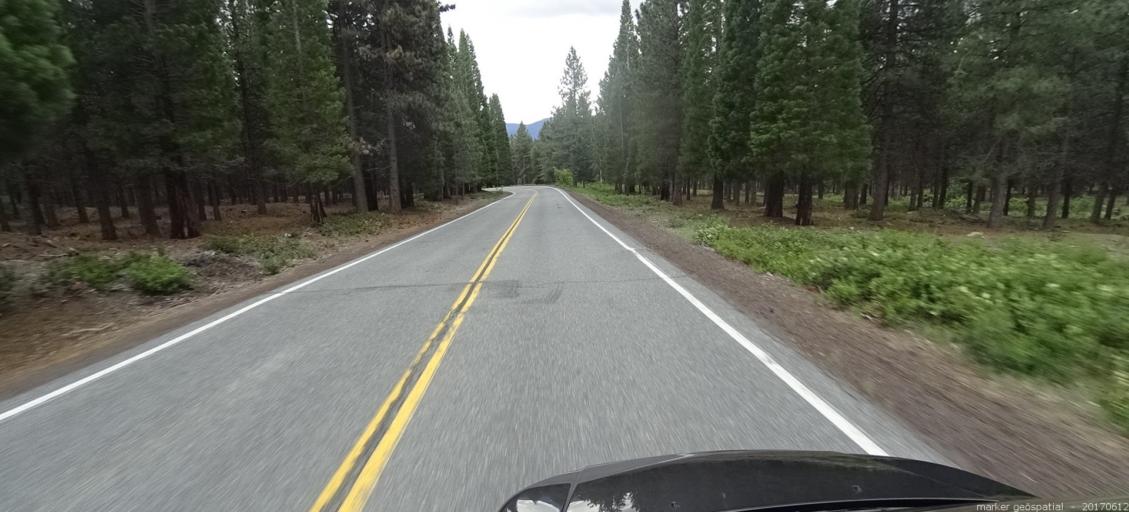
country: US
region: California
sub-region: Siskiyou County
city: Mount Shasta
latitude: 41.3421
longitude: -122.3119
